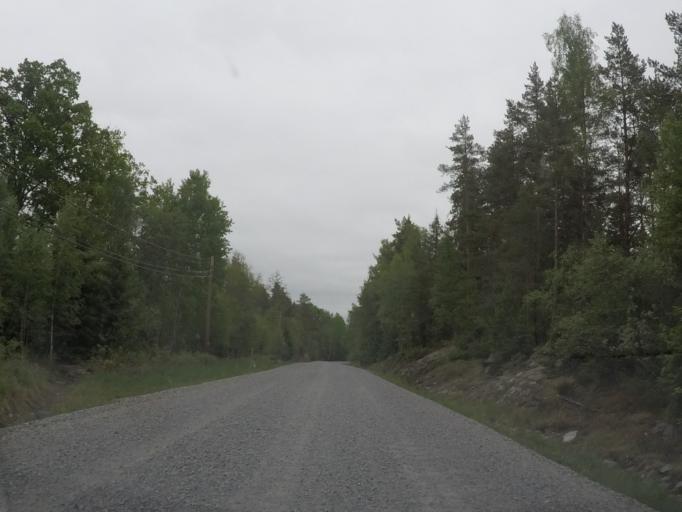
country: SE
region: Soedermanland
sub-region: Flens Kommun
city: Halleforsnas
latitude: 59.1751
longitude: 16.5044
